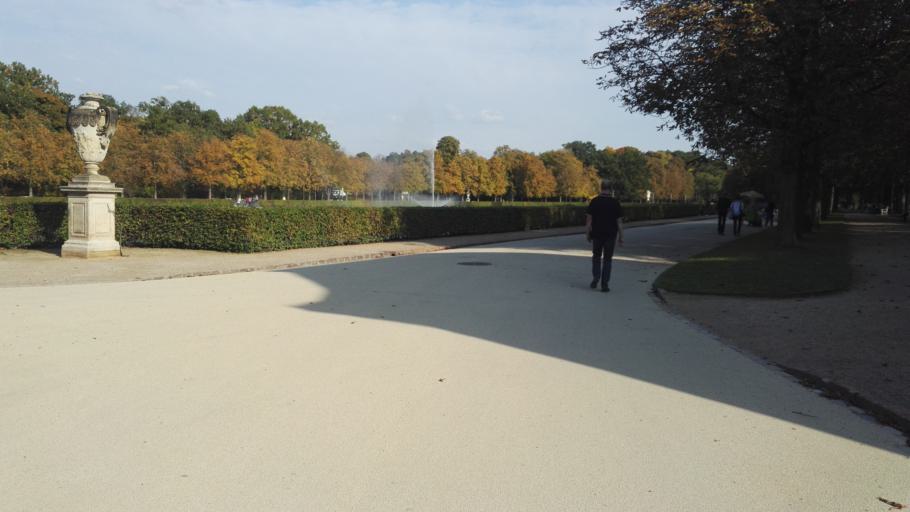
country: DE
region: Saxony
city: Dresden
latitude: 51.0372
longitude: 13.7632
